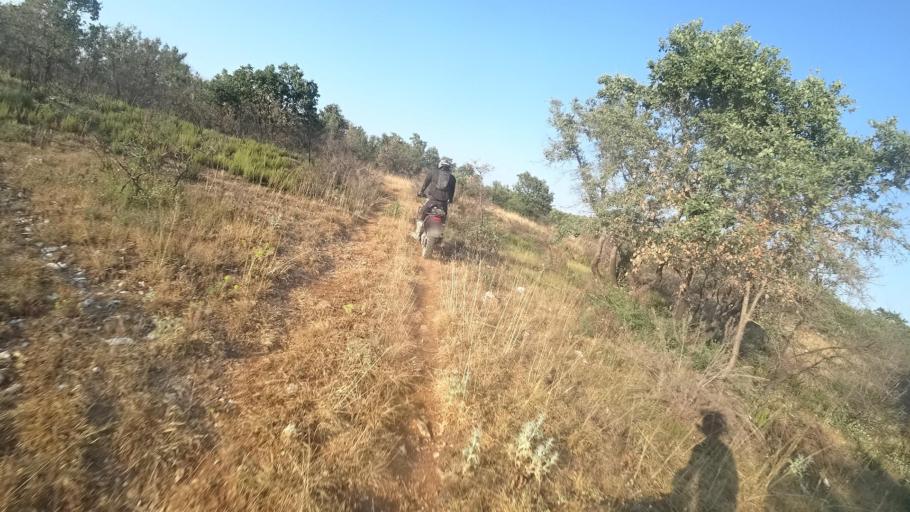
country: HR
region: Istarska
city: Galizana
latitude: 44.9518
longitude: 13.9072
